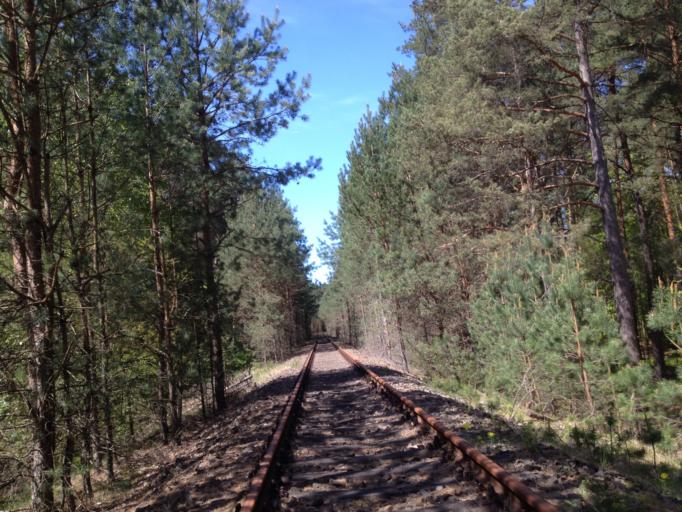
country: DE
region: Brandenburg
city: Lychen
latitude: 53.1707
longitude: 13.3607
